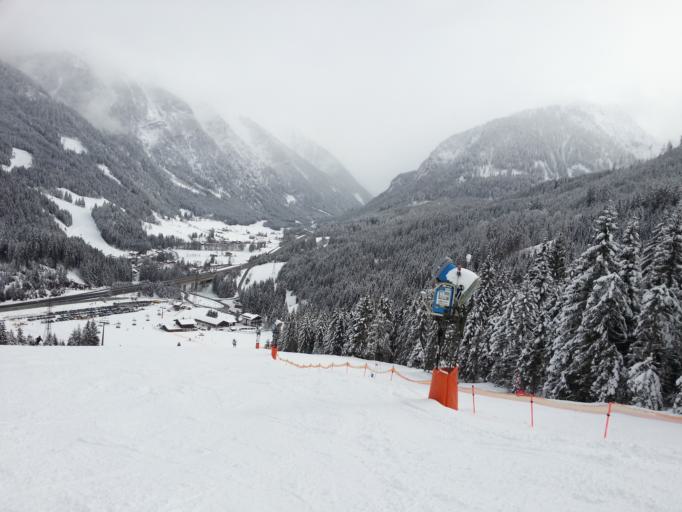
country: AT
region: Salzburg
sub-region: Politischer Bezirk Sankt Johann im Pongau
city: Flachau
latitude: 47.3009
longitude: 13.3850
